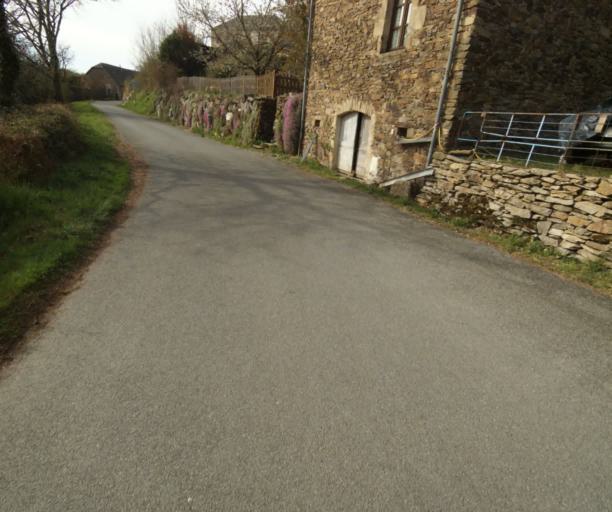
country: FR
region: Limousin
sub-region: Departement de la Correze
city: Correze
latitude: 45.4231
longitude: 1.8030
